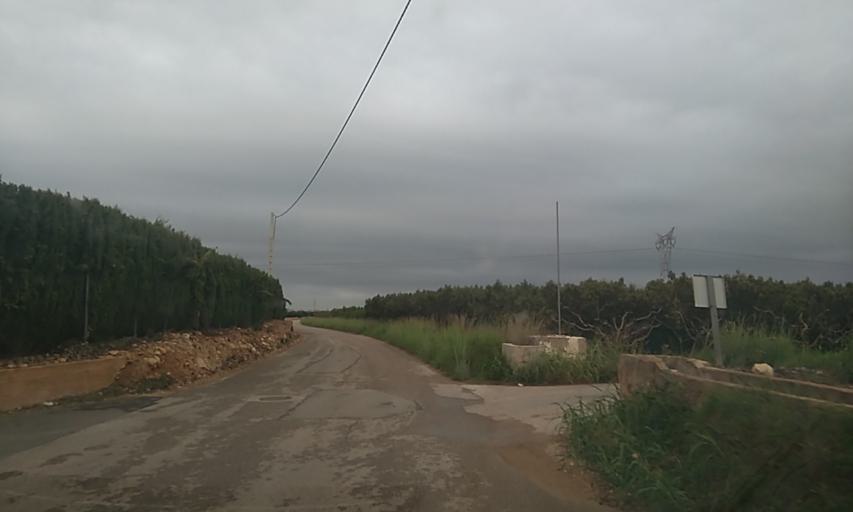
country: ES
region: Valencia
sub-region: Provincia de Valencia
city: Benimodo
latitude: 39.1883
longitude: -0.5437
